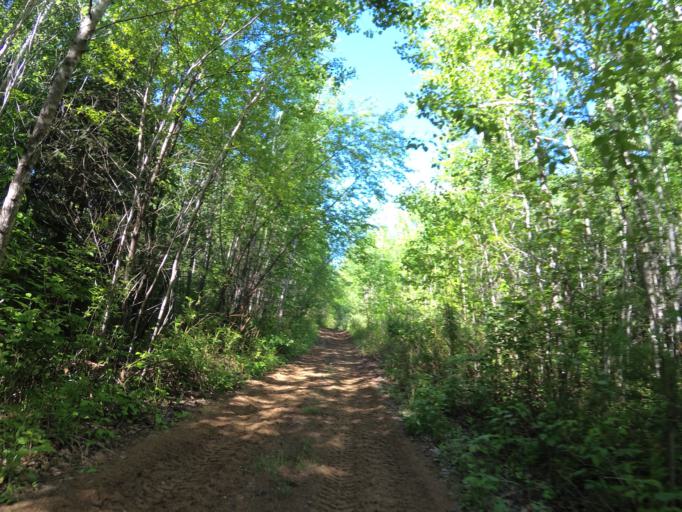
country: CA
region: Ontario
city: Renfrew
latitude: 45.1206
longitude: -77.0319
